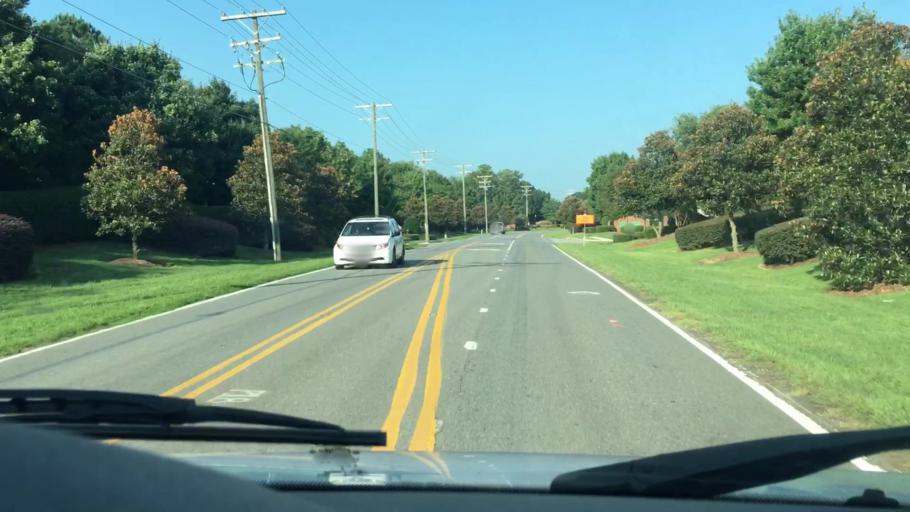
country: US
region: North Carolina
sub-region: Lincoln County
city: Lowesville
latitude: 35.4410
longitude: -80.9938
